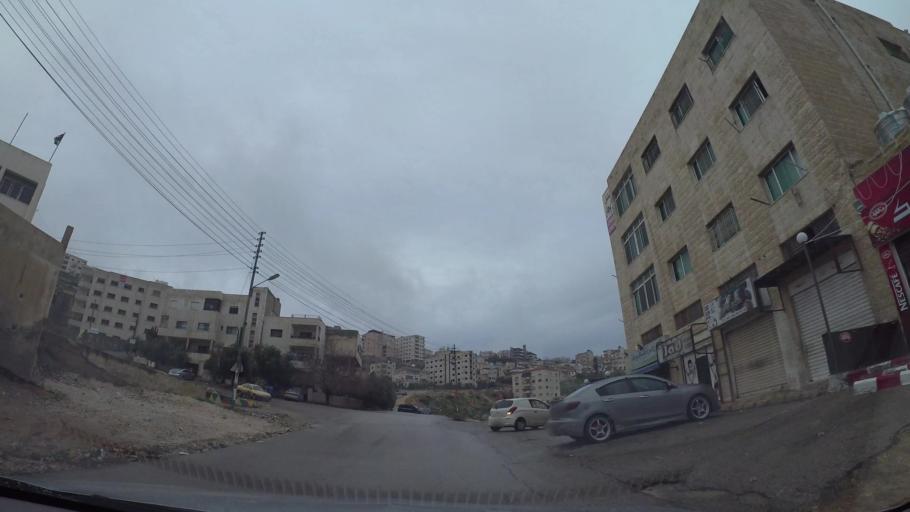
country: JO
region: Amman
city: Al Jubayhah
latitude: 32.0354
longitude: 35.8293
